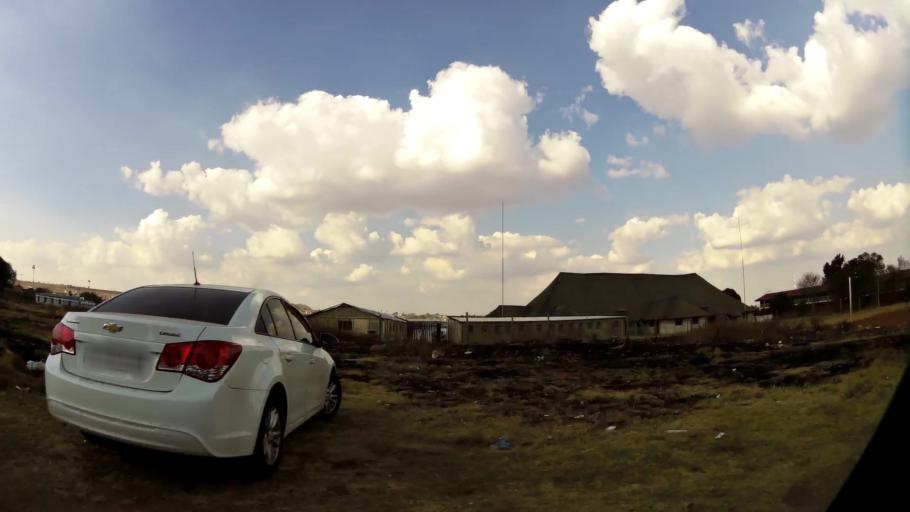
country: ZA
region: Gauteng
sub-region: City of Johannesburg Metropolitan Municipality
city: Roodepoort
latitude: -26.2127
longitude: 27.8663
